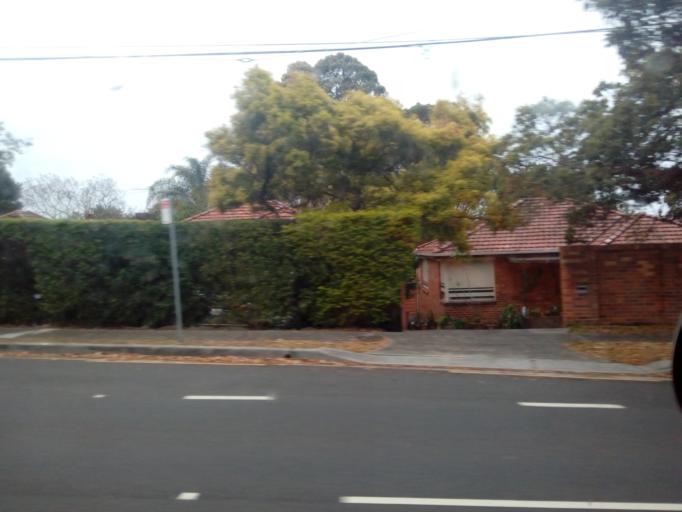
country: AU
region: New South Wales
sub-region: Willoughby
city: Castle Cove
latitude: -33.7953
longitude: 151.2086
